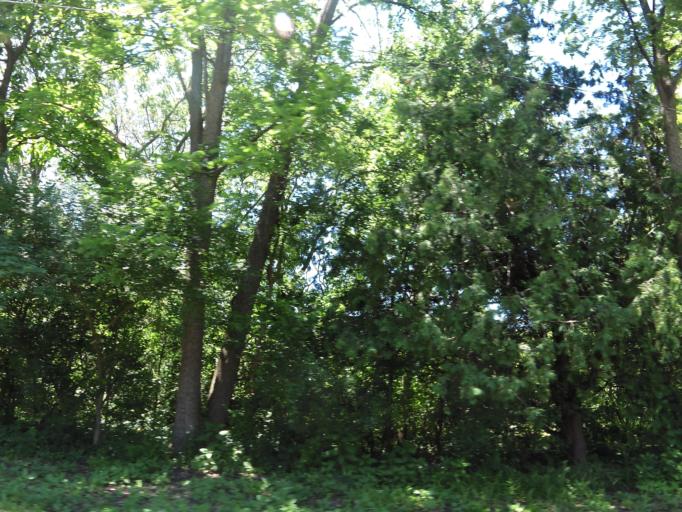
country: US
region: Illinois
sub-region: Livingston County
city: Chatsworth
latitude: 40.7576
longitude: -88.1851
